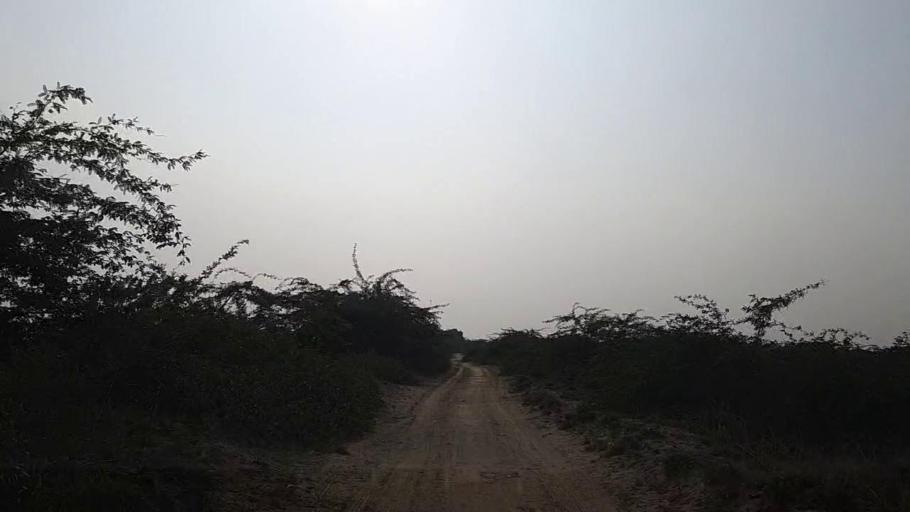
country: PK
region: Sindh
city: Gharo
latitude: 24.6590
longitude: 67.6244
